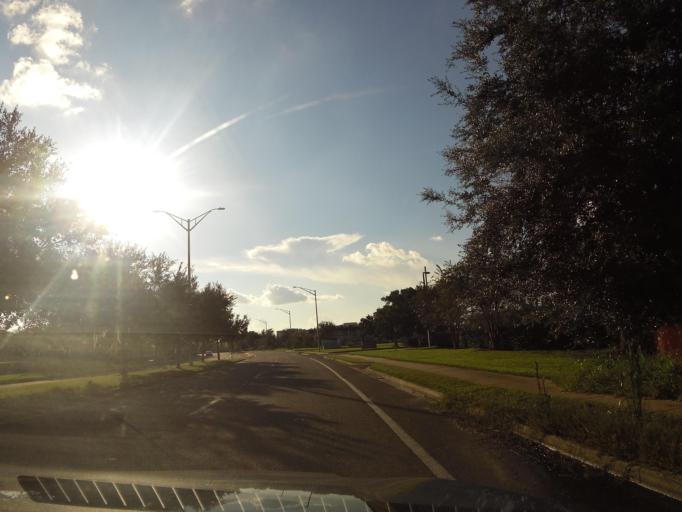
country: US
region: Florida
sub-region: Duval County
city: Jacksonville
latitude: 30.2491
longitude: -81.5776
